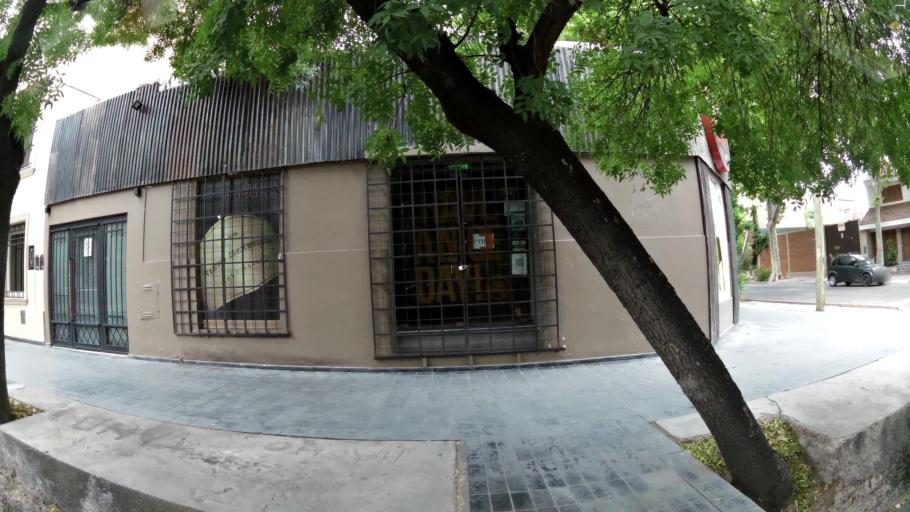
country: AR
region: Mendoza
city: Mendoza
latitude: -32.8912
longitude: -68.8606
